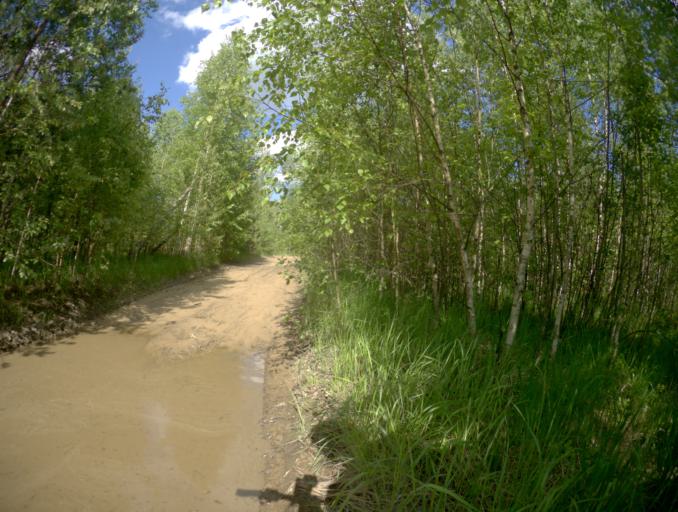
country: RU
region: Vladimir
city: Zolotkovo
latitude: 55.3299
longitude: 40.9627
